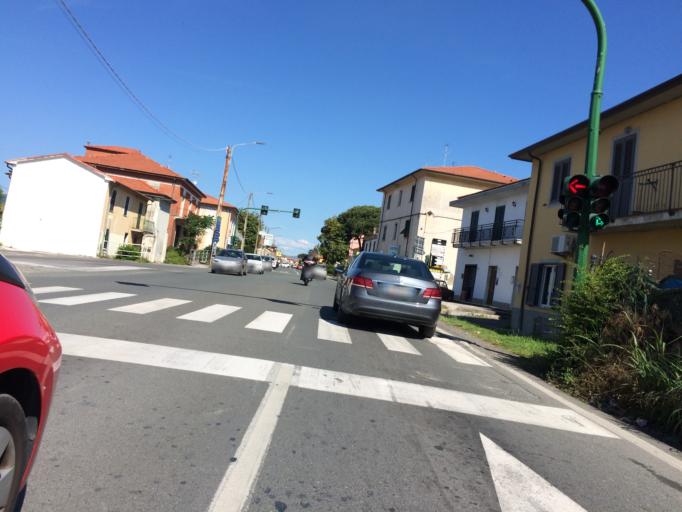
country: IT
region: Liguria
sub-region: Provincia di La Spezia
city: Casano-Dogana-Isola
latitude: 44.0659
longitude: 10.0320
